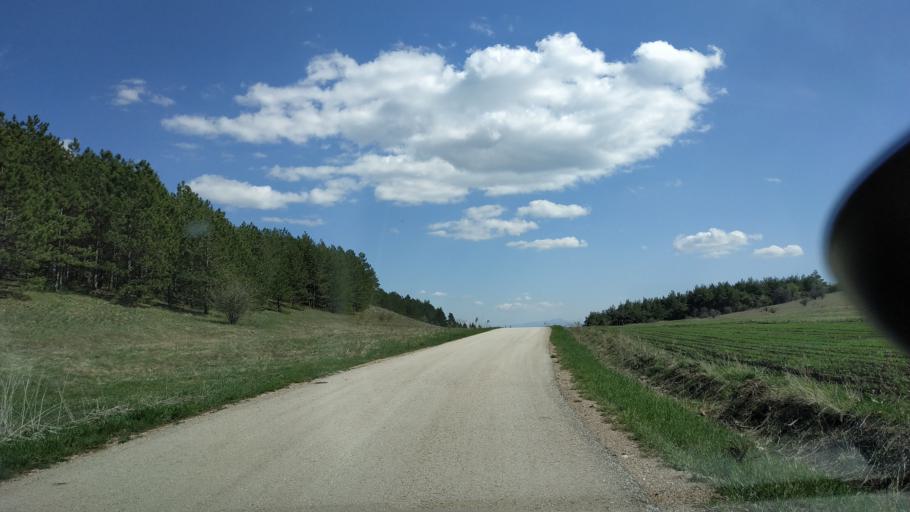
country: RS
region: Central Serbia
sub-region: Zajecarski Okrug
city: Soko Banja
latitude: 43.5926
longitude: 21.8865
